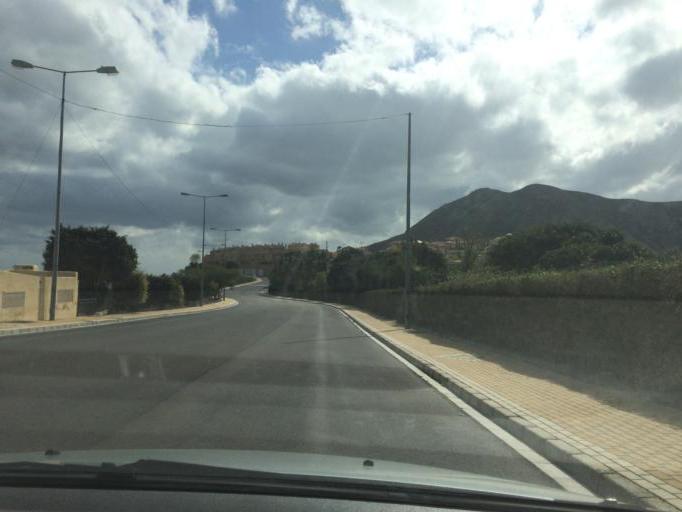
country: ES
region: Andalusia
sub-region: Provincia de Almeria
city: Vicar
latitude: 36.8378
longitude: -2.6138
